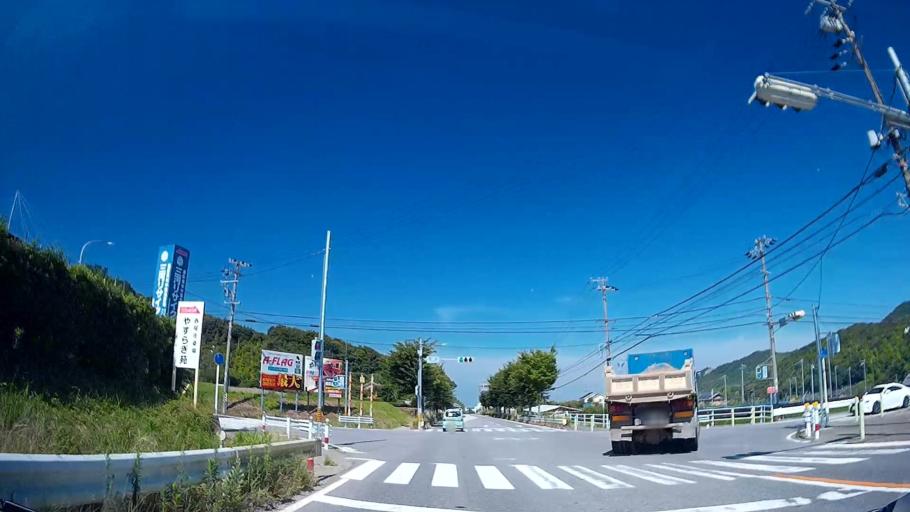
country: JP
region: Aichi
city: Nishio
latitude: 34.8284
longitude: 137.1253
